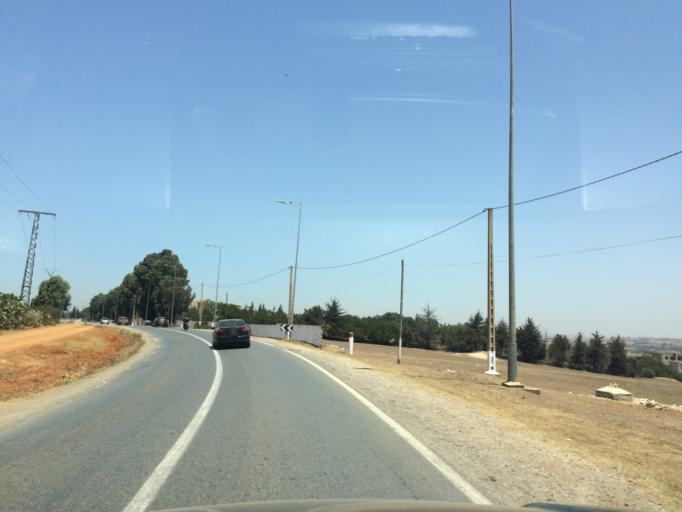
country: MA
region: Rabat-Sale-Zemmour-Zaer
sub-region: Skhirate-Temara
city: Temara
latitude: 33.8784
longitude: -6.8452
